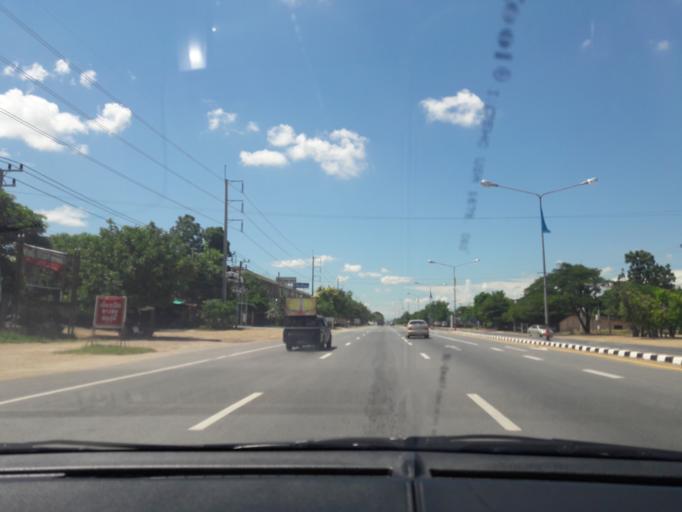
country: TH
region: Kanchanaburi
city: Tha Maka
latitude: 14.0403
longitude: 99.7891
